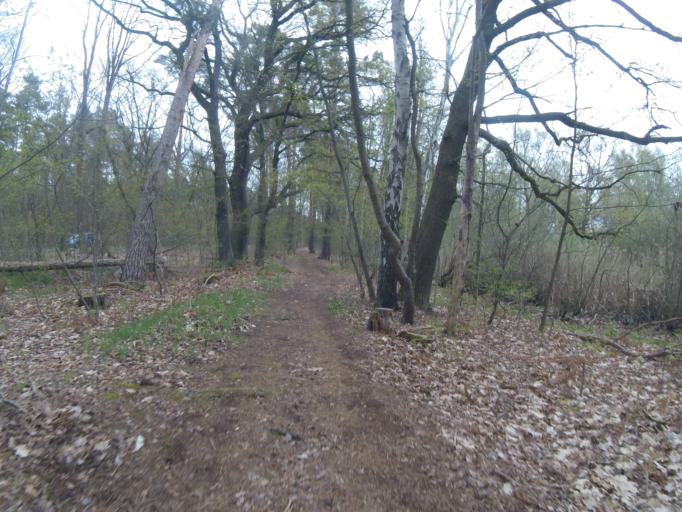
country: DE
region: Brandenburg
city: Bestensee
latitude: 52.2423
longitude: 13.6770
